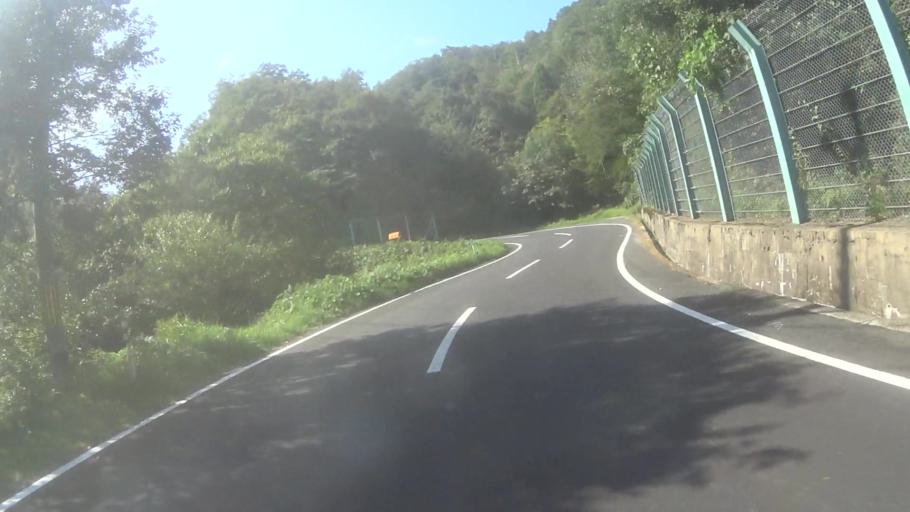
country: JP
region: Kyoto
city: Miyazu
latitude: 35.6941
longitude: 135.1457
